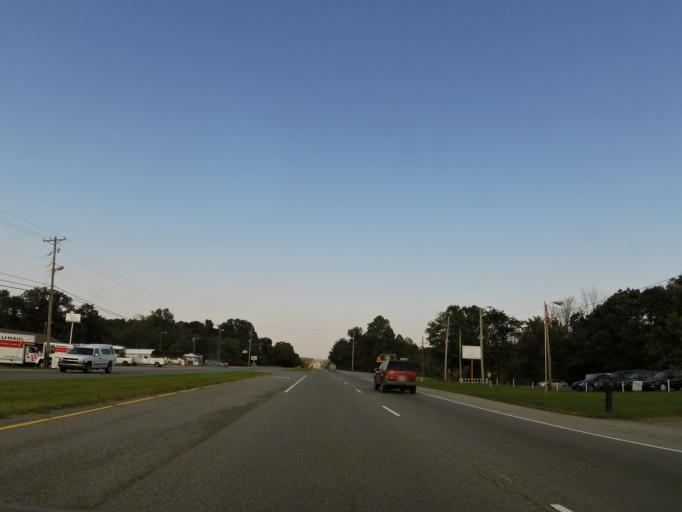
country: US
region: Tennessee
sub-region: Knox County
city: Mascot
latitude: 36.0200
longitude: -83.7923
